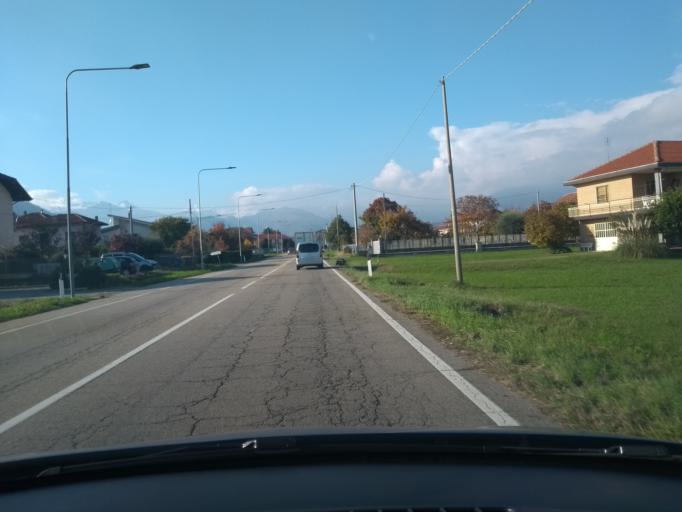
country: IT
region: Piedmont
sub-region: Provincia di Torino
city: Balangero
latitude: 45.2637
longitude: 7.5276
